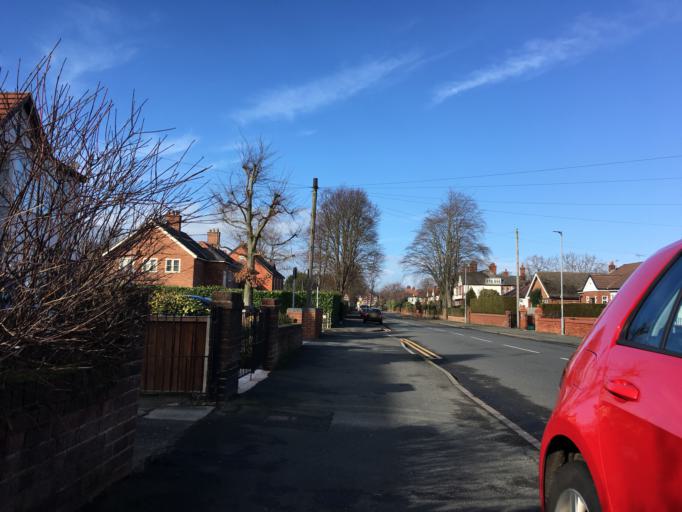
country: GB
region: England
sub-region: Cheshire West and Chester
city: Hoole
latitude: 53.2000
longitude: -2.8674
